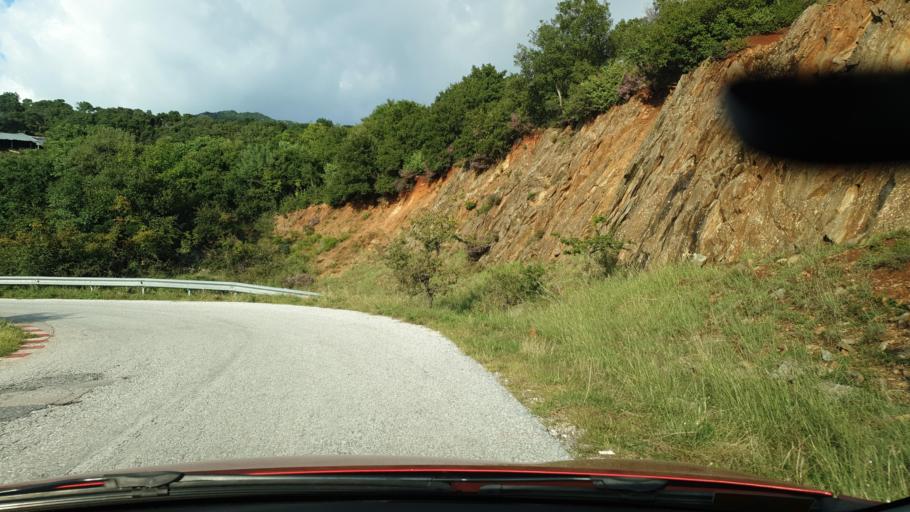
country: GR
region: Central Macedonia
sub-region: Nomos Thessalonikis
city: Peristera
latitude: 40.5197
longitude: 23.1883
